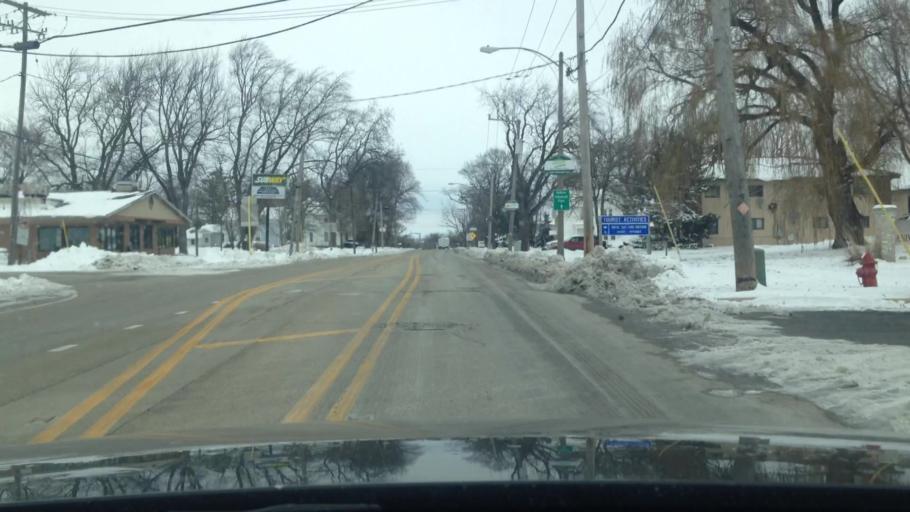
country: US
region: Illinois
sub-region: McHenry County
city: Hebron
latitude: 42.4725
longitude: -88.4327
